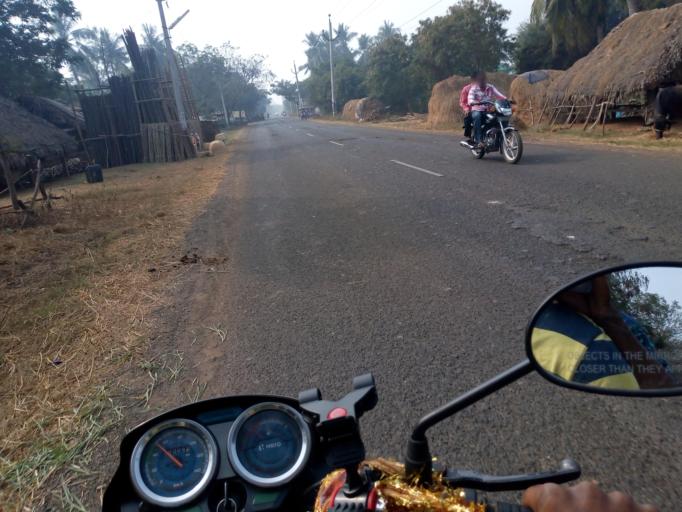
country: IN
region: Andhra Pradesh
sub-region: West Godavari
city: Tadepallegudem
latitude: 16.7545
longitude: 81.4233
